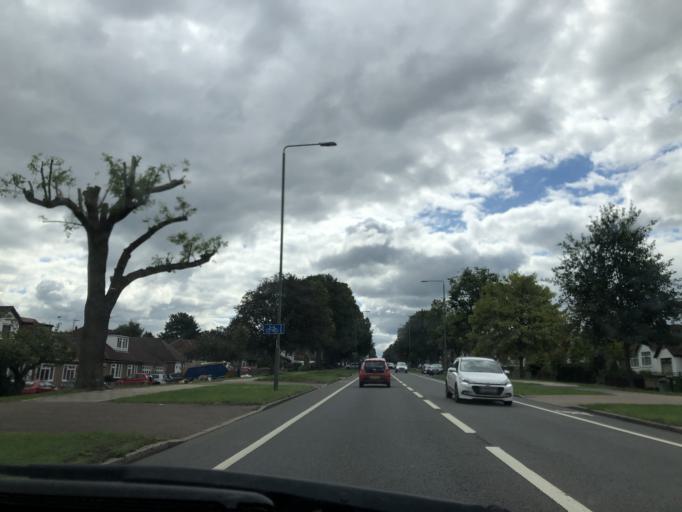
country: GB
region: England
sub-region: Greater London
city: Orpington
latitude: 51.3758
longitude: 0.1091
